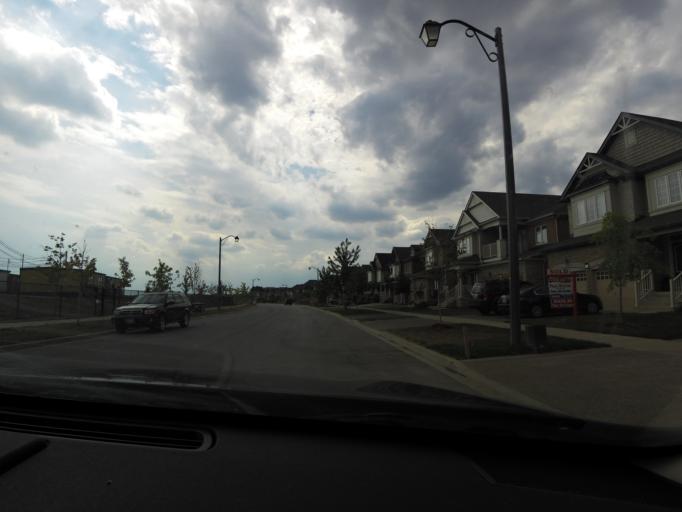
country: CA
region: Ontario
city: Brampton
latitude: 43.7584
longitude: -79.8254
